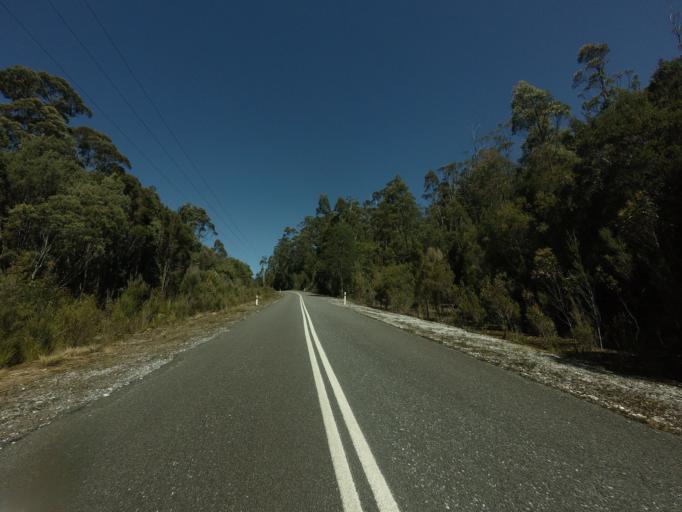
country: AU
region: Tasmania
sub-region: West Coast
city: Queenstown
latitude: -42.7617
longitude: 146.0048
